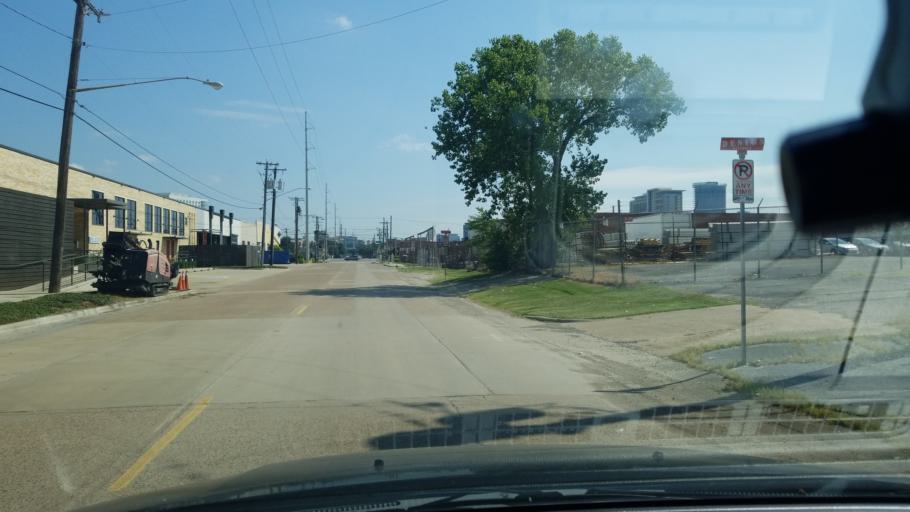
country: US
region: Texas
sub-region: Dallas County
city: Dallas
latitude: 32.7907
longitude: -96.8243
